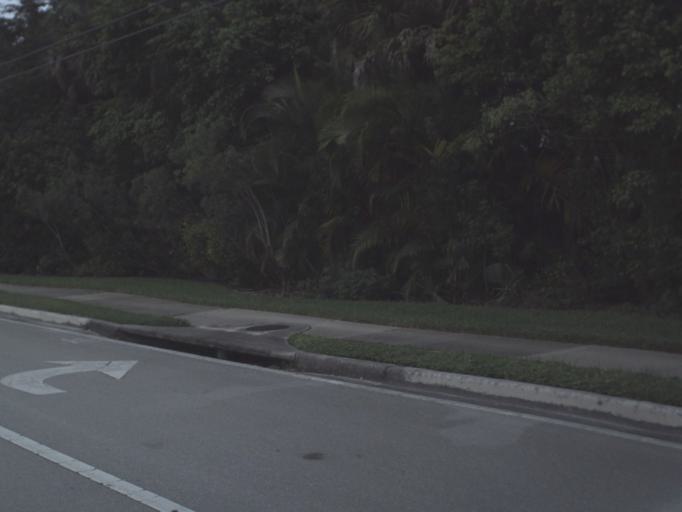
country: US
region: Florida
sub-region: Collier County
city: Lely Resort
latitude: 26.1138
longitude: -81.6872
